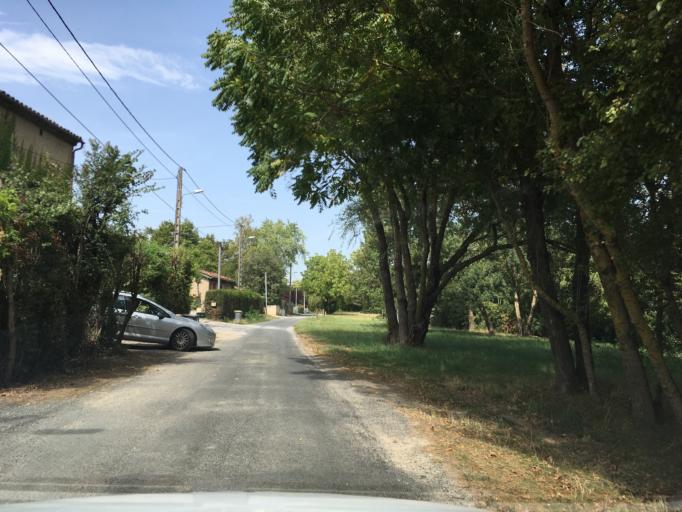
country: FR
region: Midi-Pyrenees
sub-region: Departement du Tarn
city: Castres
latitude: 43.6133
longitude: 2.2254
